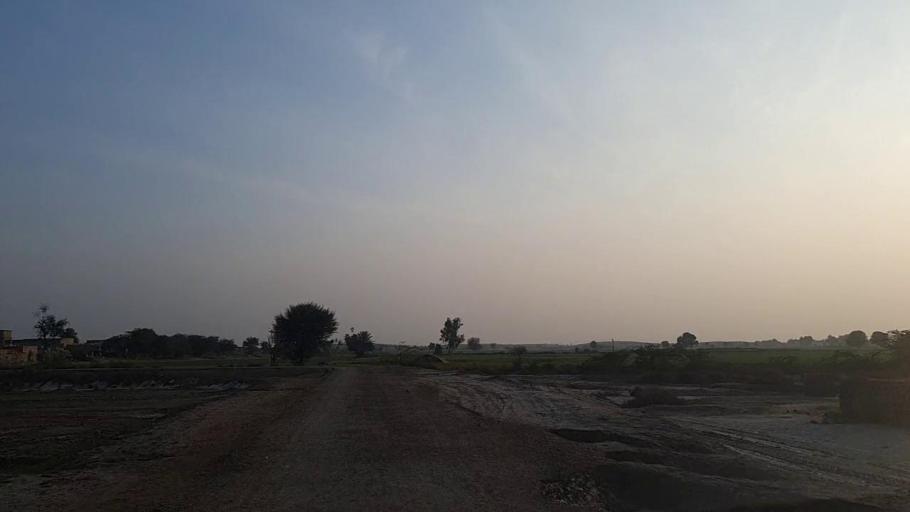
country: PK
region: Sindh
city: Jam Sahib
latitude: 26.4101
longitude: 68.6056
